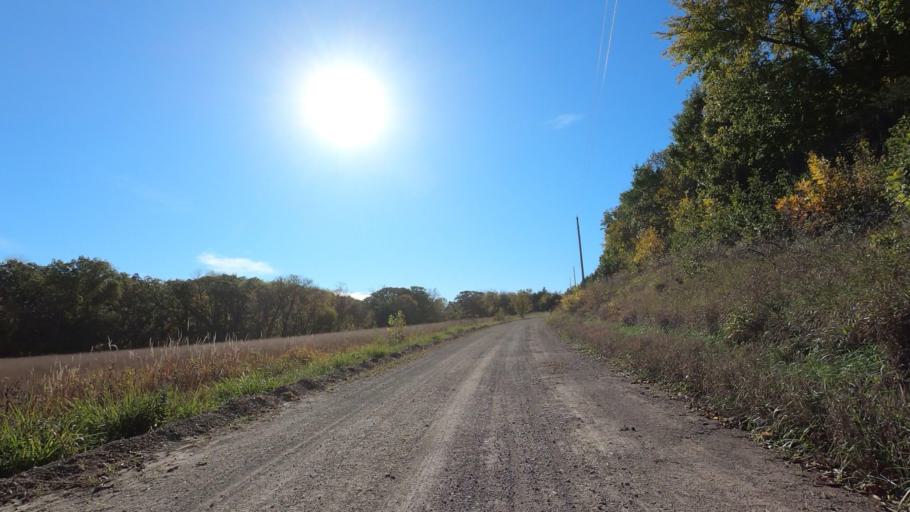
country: US
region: Kansas
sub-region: Marshall County
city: Blue Rapids
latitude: 39.4886
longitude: -96.6045
